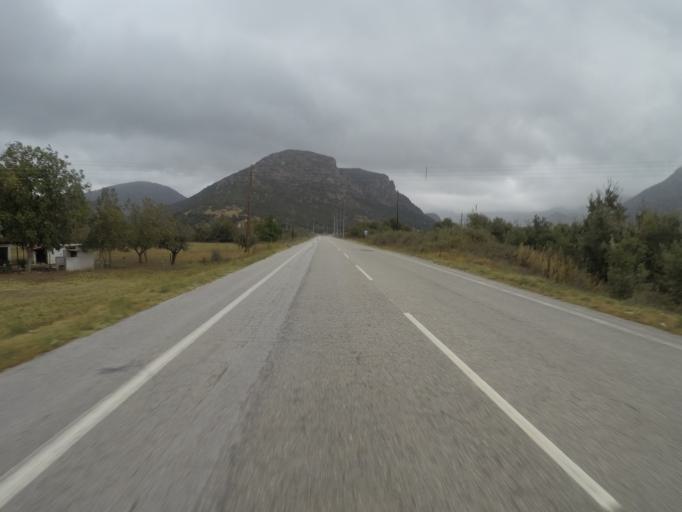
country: GR
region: Peloponnese
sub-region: Nomos Arkadias
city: Tripoli
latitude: 37.5900
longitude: 22.4275
